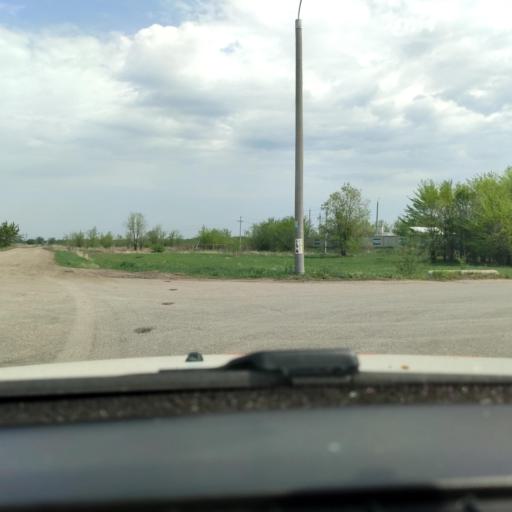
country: RU
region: Samara
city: Krasnyy Yar
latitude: 53.4463
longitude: 50.3745
